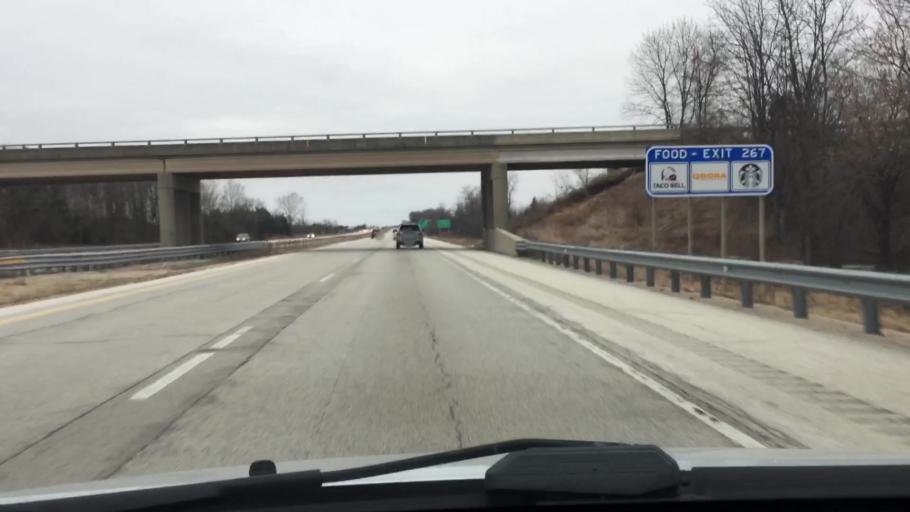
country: US
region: Wisconsin
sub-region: Jefferson County
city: Johnson Creek
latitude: 43.0866
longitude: -88.7341
